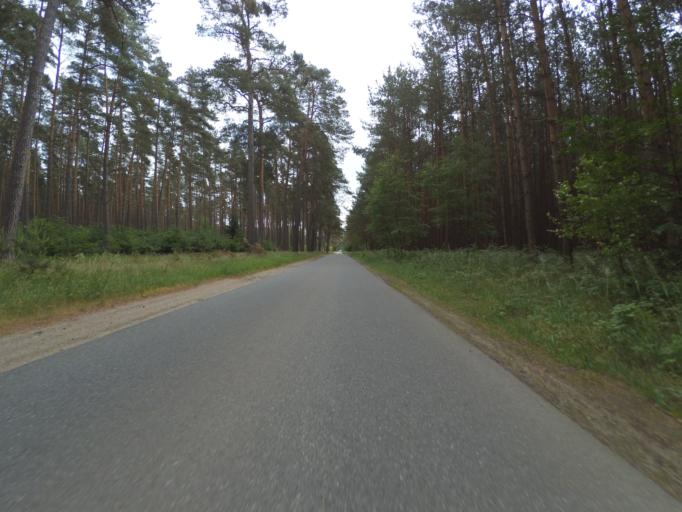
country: DE
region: Mecklenburg-Vorpommern
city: Malchow
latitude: 53.5602
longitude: 12.3974
